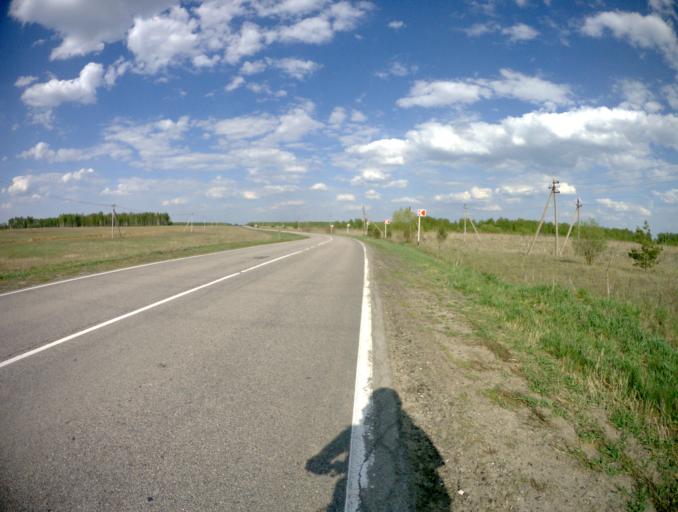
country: RU
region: Vladimir
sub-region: Kovrovskiy Rayon
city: Kovrov
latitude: 56.4519
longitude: 41.3348
